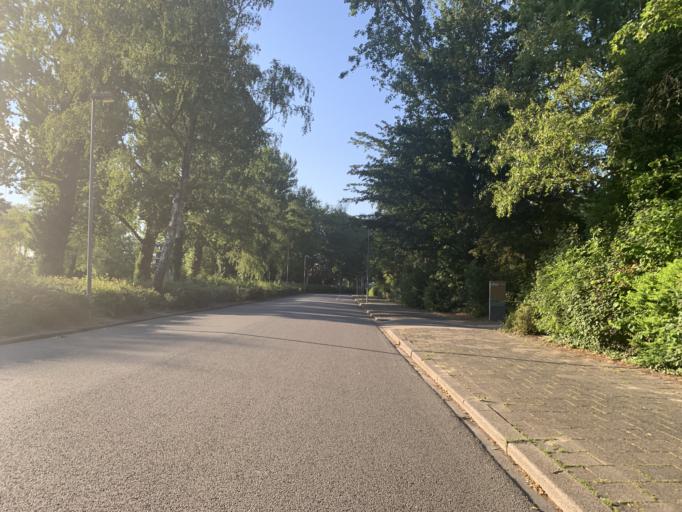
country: NL
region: Groningen
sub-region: Gemeente Groningen
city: Oosterpark
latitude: 53.2034
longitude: 6.5837
